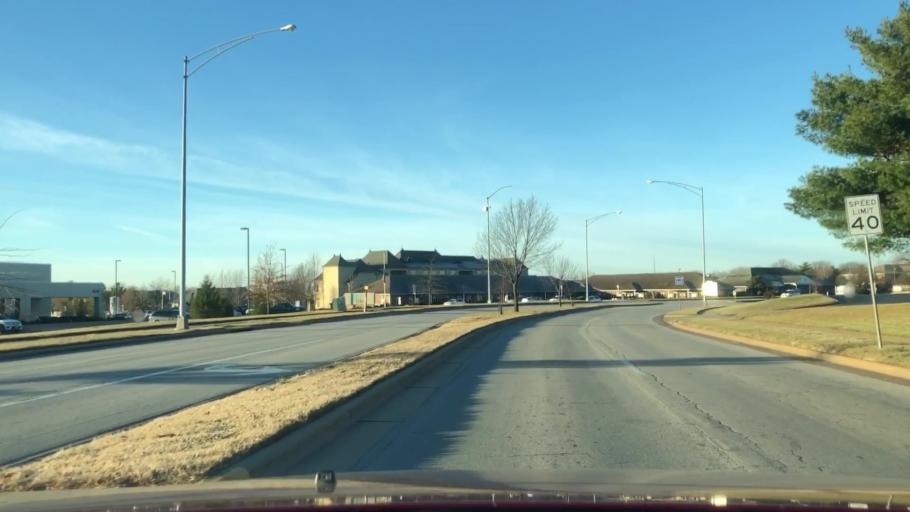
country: US
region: Missouri
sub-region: Greene County
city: Springfield
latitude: 37.1475
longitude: -93.2664
